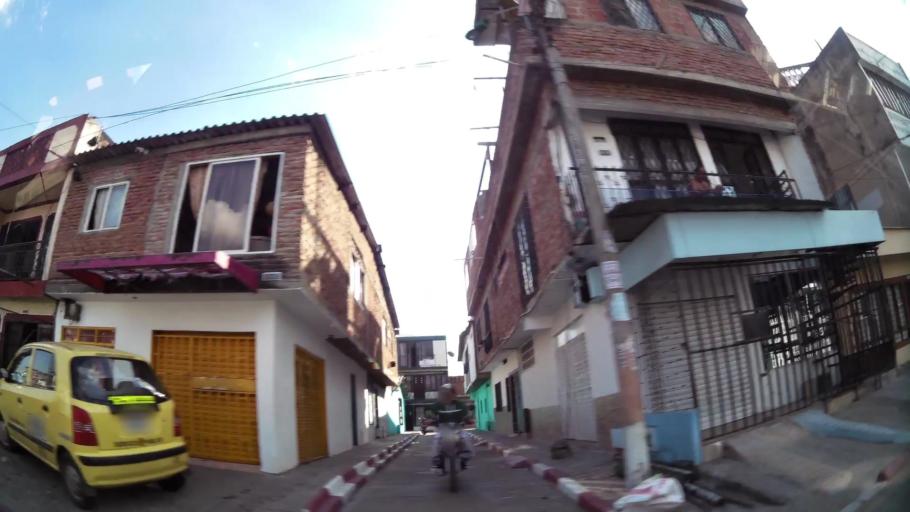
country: CO
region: Valle del Cauca
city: Cali
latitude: 3.4172
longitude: -76.4987
